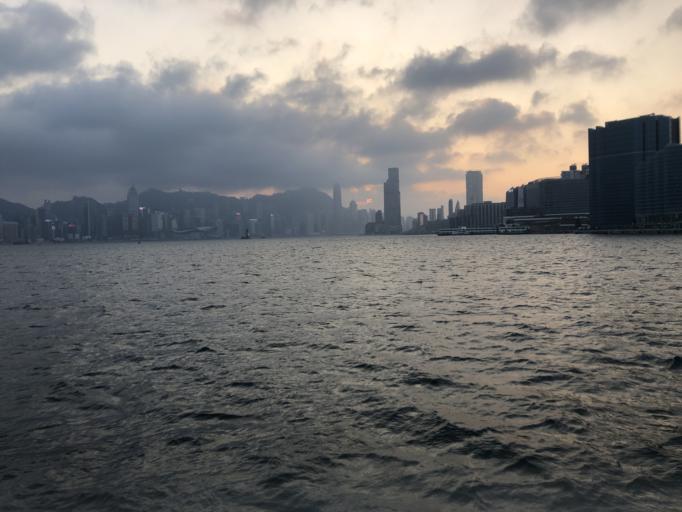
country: HK
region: Kowloon City
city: Kowloon
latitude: 22.3020
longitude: 114.1971
